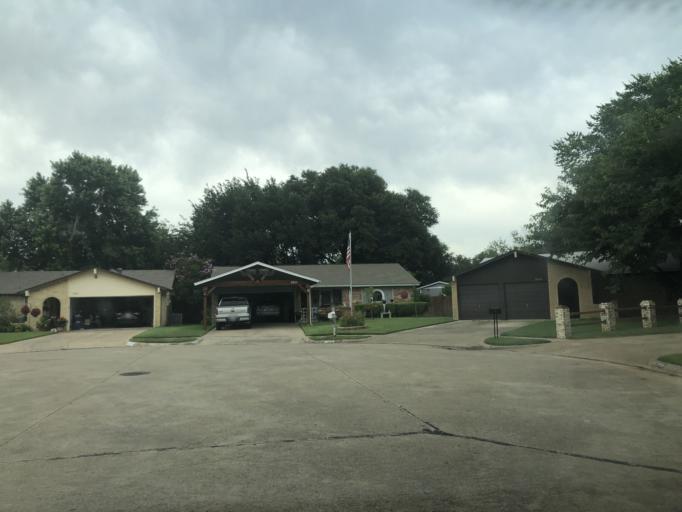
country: US
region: Texas
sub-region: Dallas County
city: Irving
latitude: 32.7834
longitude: -96.9670
